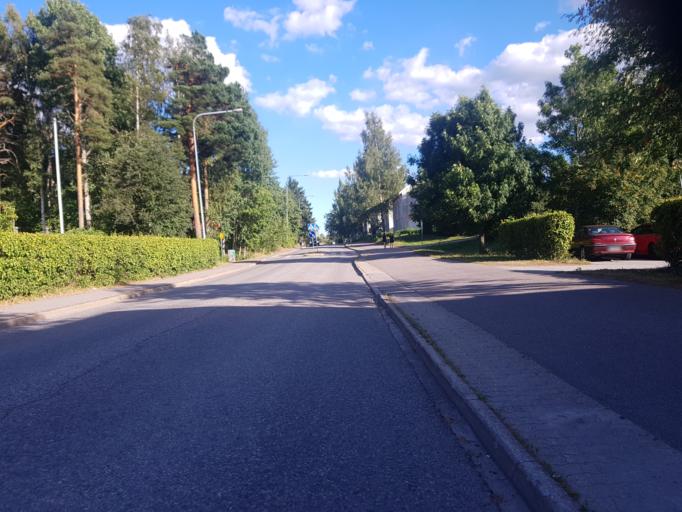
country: FI
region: Uusimaa
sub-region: Helsinki
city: Vantaa
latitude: 60.2714
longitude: 25.0055
